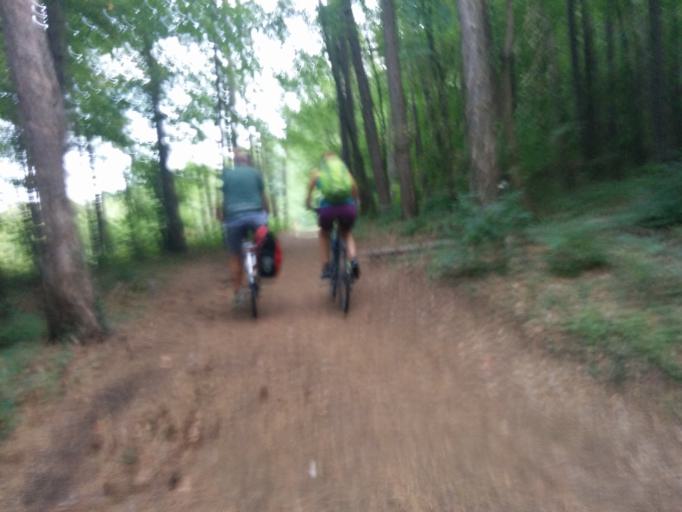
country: AT
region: Lower Austria
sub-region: Politischer Bezirk Modling
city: Gumpoldskirchen
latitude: 48.0525
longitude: 16.2669
